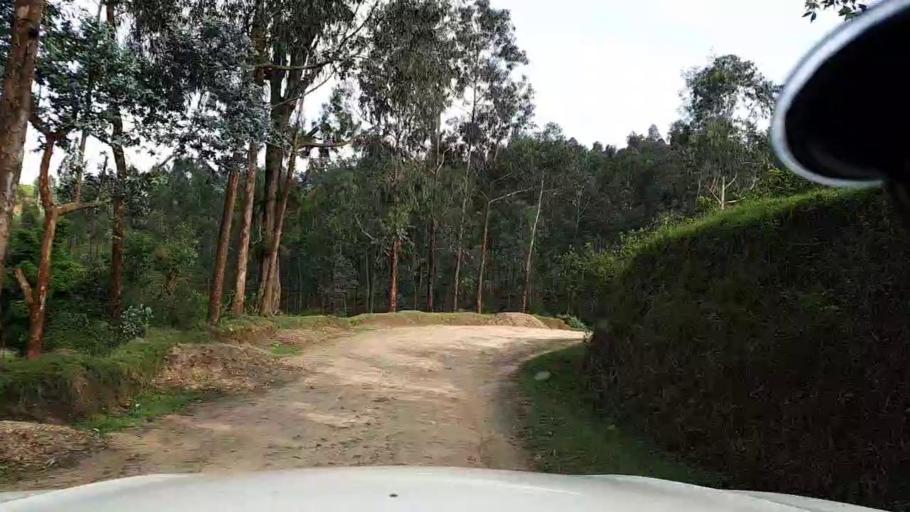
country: RW
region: Western Province
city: Kibuye
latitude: -2.1568
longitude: 29.5461
